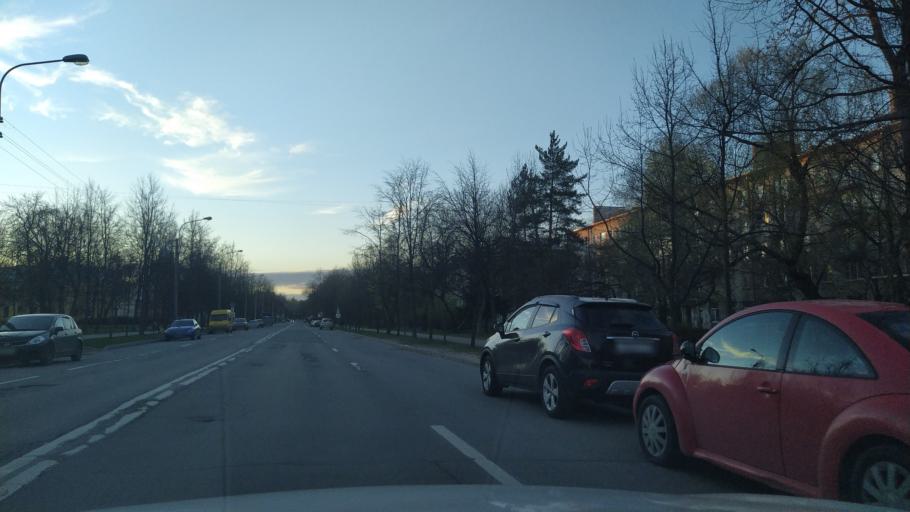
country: RU
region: St.-Petersburg
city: Pushkin
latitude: 59.7043
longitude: 30.4067
